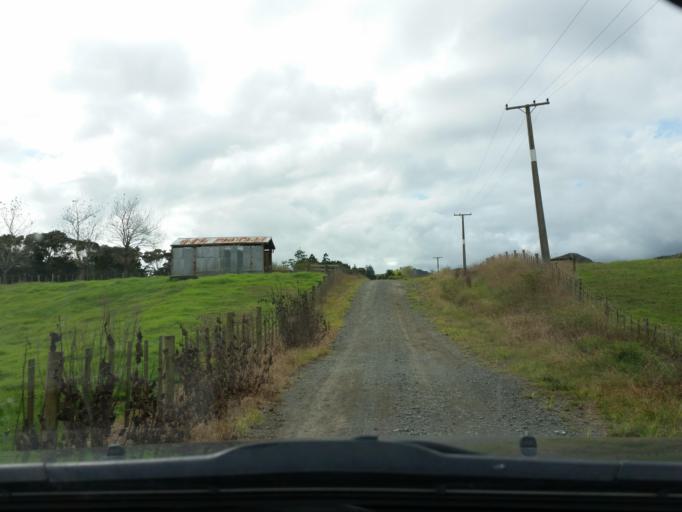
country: NZ
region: Northland
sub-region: Whangarei
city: Maungatapere
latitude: -35.7987
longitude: 174.0540
